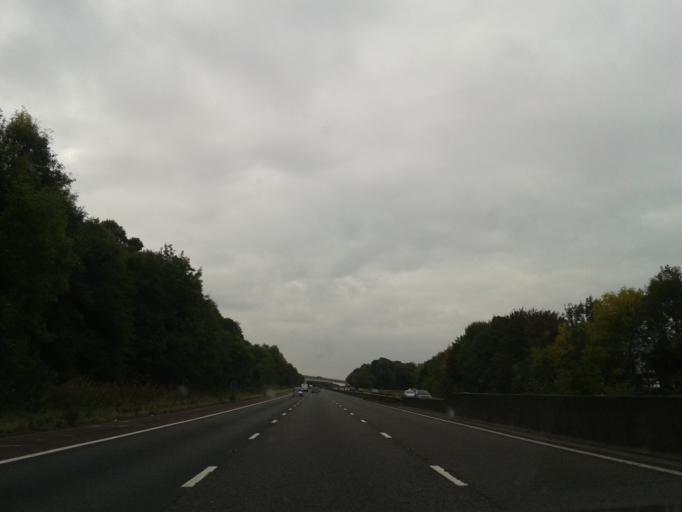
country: GB
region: England
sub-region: Lancashire
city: Bay Horse
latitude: 53.9385
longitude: -2.7564
